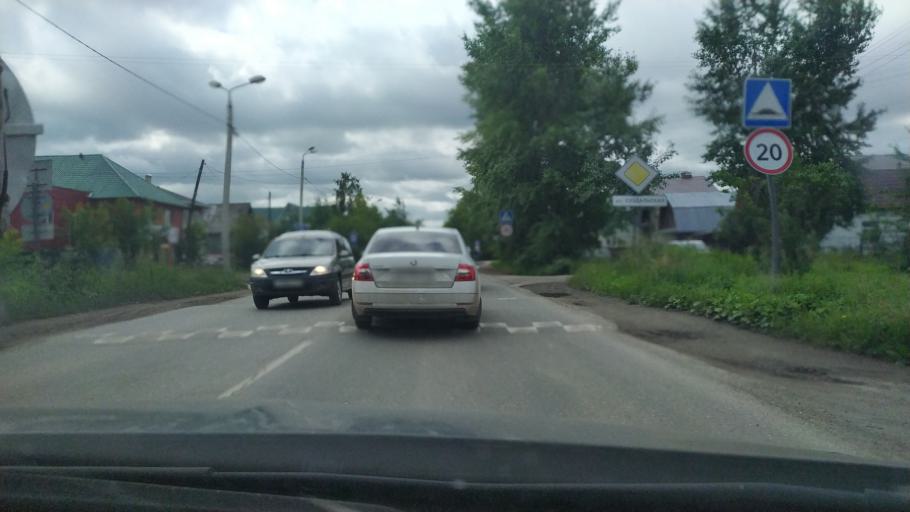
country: RU
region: Perm
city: Perm
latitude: 57.9822
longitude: 56.3047
